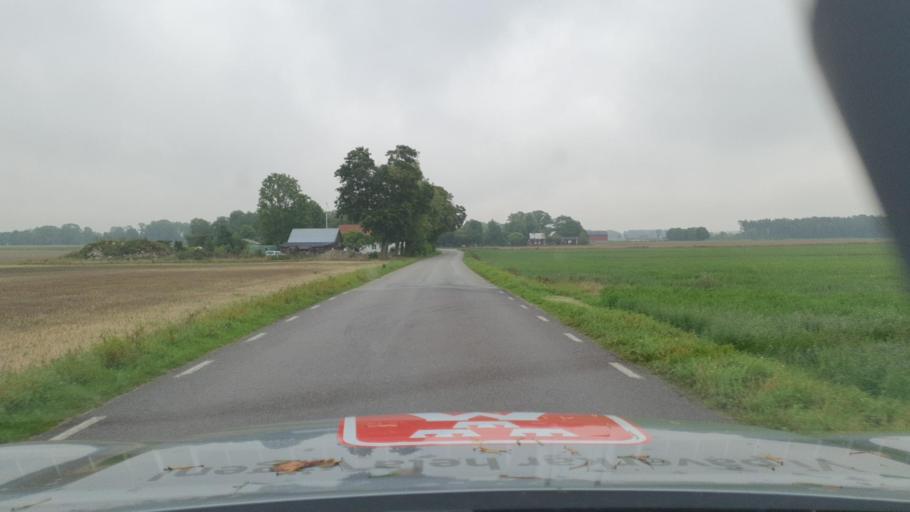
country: SE
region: Gotland
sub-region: Gotland
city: Visby
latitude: 57.7495
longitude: 18.5025
